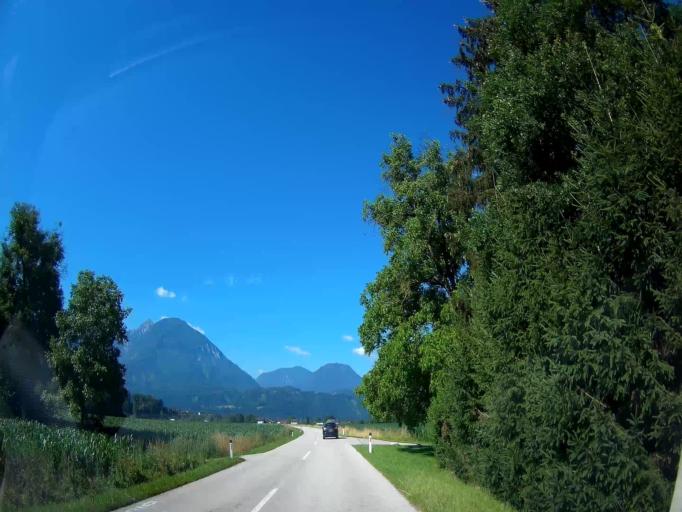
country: AT
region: Carinthia
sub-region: Politischer Bezirk Volkermarkt
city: Gallizien
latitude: 46.5860
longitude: 14.5152
